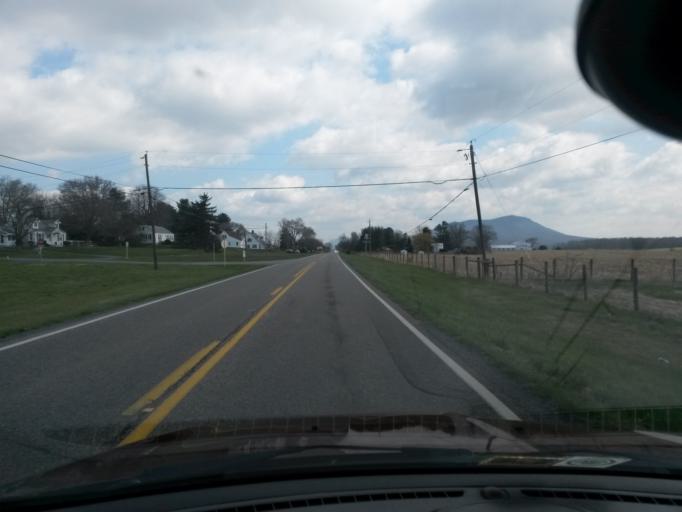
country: US
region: Virginia
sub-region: Rockingham County
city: Massanetta Springs
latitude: 38.3561
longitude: -78.8458
